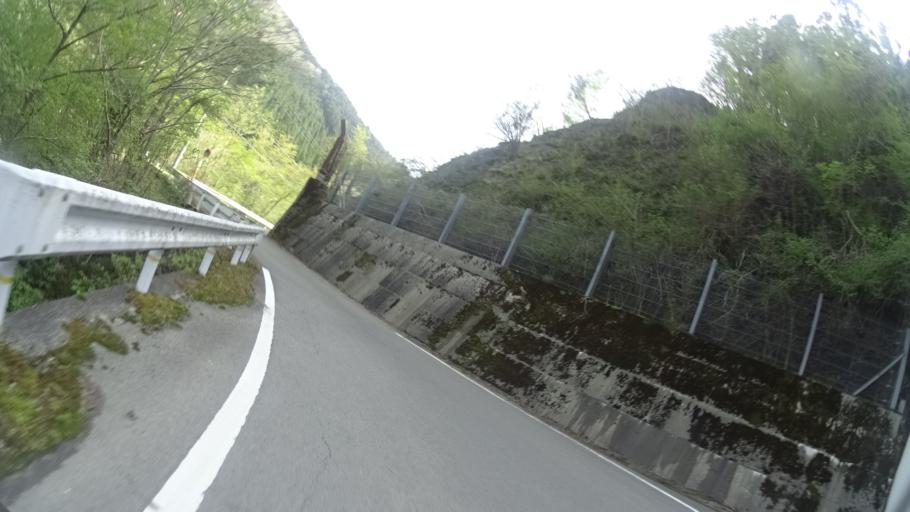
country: JP
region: Tokushima
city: Wakimachi
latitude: 33.8533
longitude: 134.0341
